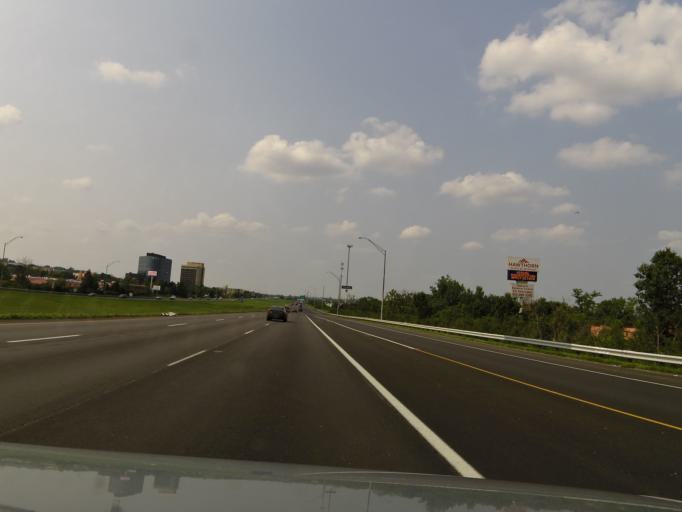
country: US
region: Ohio
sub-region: Hamilton County
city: Glendale
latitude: 39.2733
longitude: -84.4402
